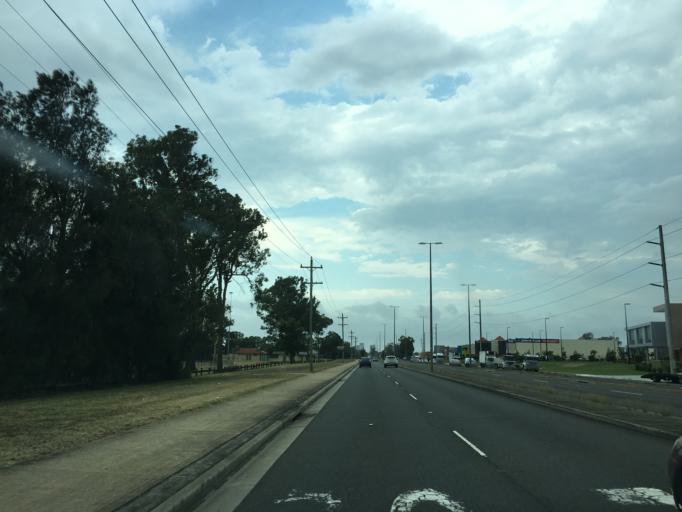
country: AU
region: New South Wales
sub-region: Liverpool
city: Miller
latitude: -33.9277
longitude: 150.8762
